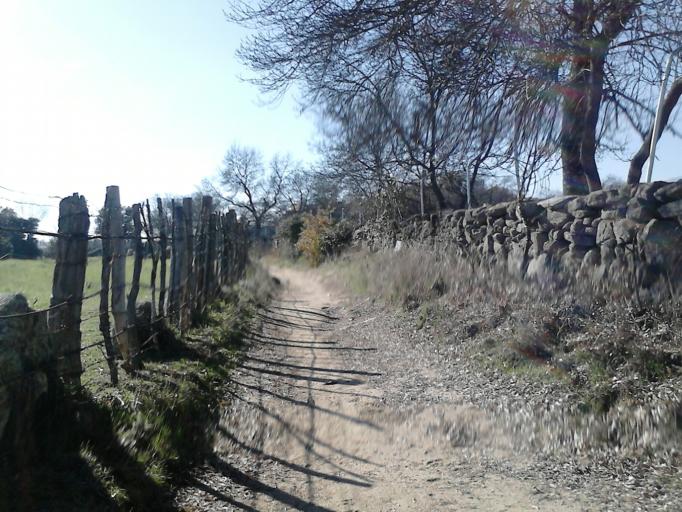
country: ES
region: Madrid
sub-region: Provincia de Madrid
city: El Escorial
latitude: 40.6070
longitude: -4.0935
